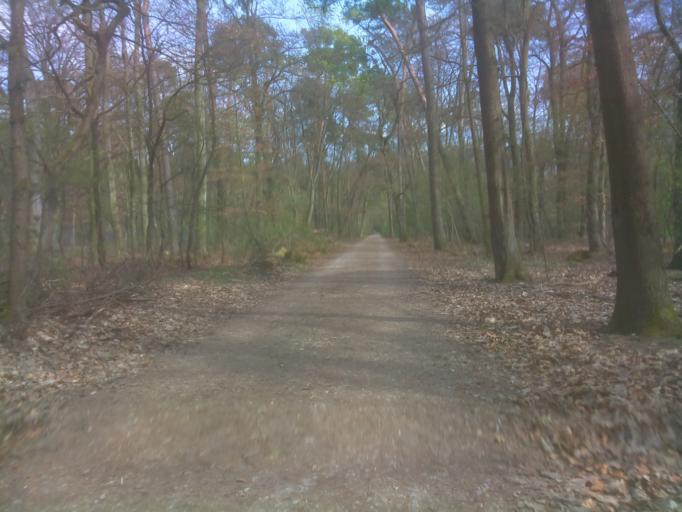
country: DE
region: Baden-Wuerttemberg
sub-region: Karlsruhe Region
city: Mannheim
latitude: 49.5310
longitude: 8.5183
